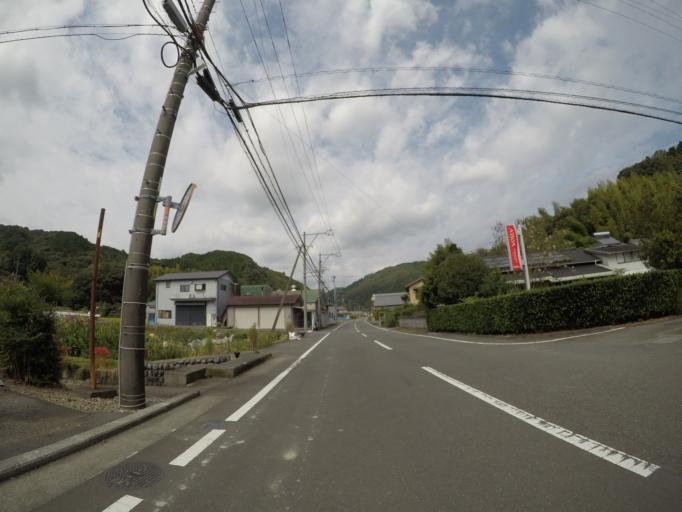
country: JP
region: Shizuoka
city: Shimada
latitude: 34.8670
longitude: 138.1831
